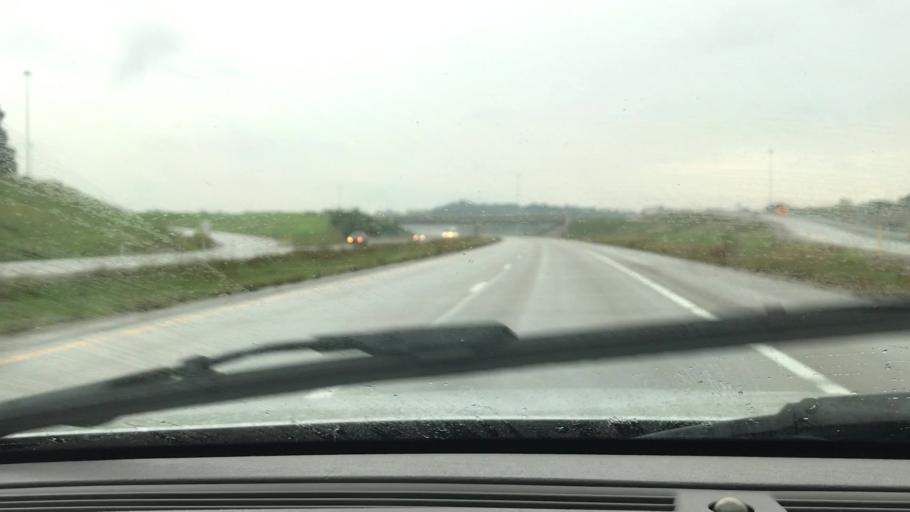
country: US
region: Kentucky
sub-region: Barren County
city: Glasgow
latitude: 36.9936
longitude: -85.9846
